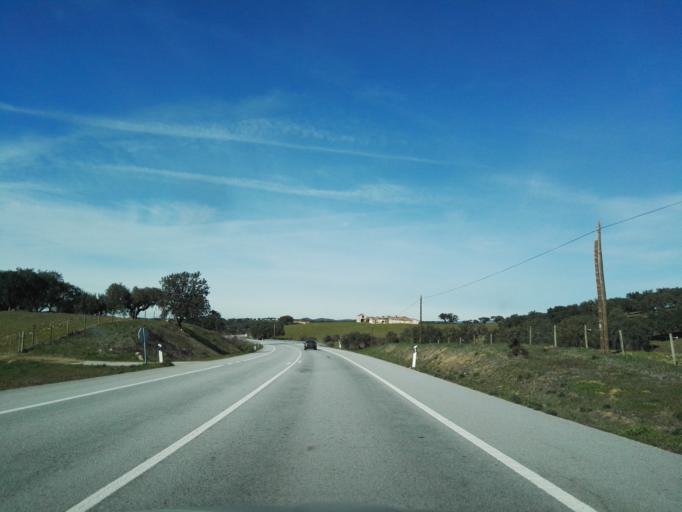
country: PT
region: Portalegre
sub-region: Portalegre
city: Alegrete
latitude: 39.1781
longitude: -7.3410
